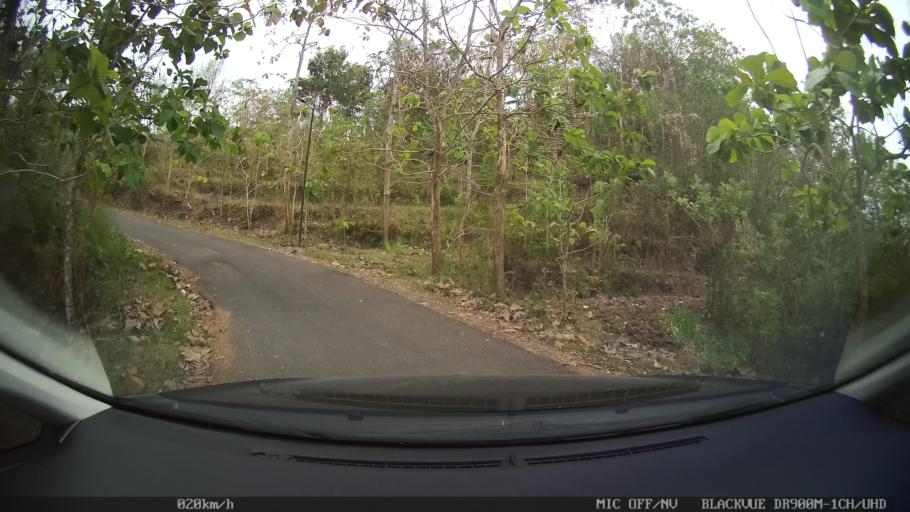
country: ID
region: Central Java
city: Candi Prambanan
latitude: -7.7957
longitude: 110.5212
